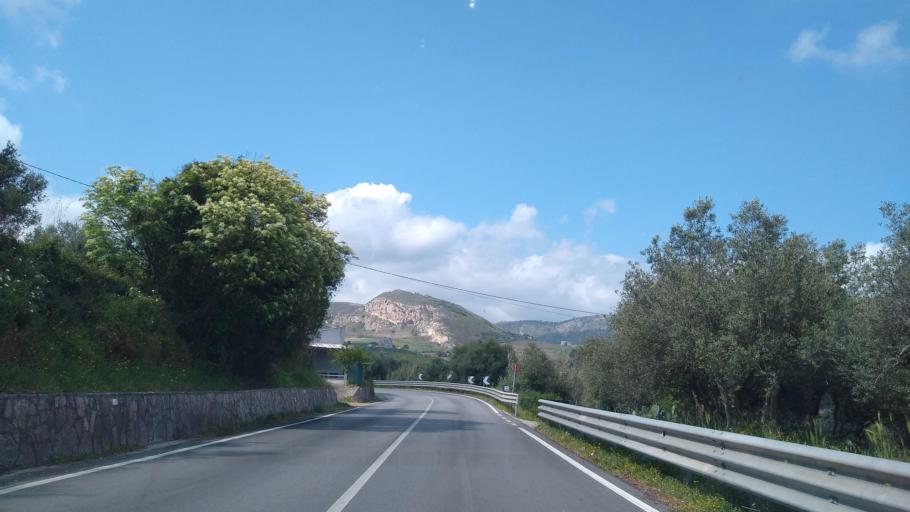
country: IT
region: Sicily
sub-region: Trapani
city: Calatafimi
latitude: 37.9539
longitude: 12.8649
